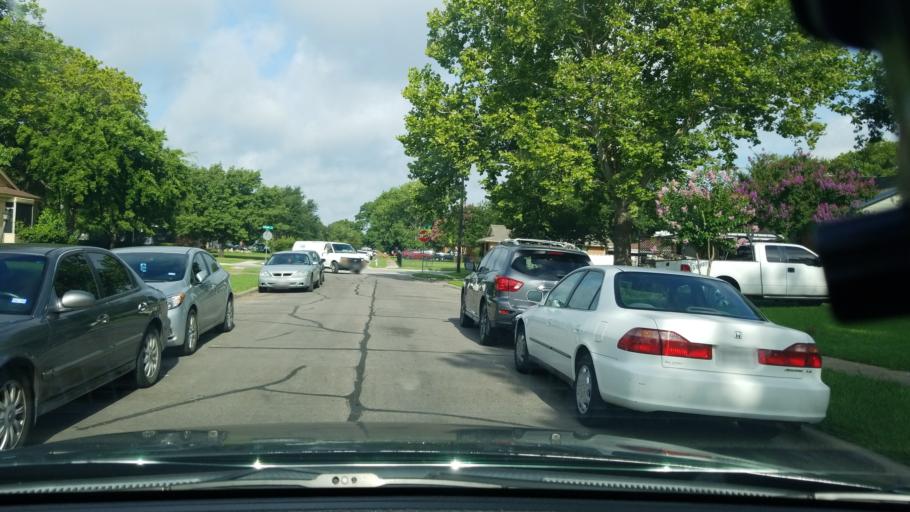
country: US
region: Texas
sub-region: Dallas County
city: Mesquite
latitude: 32.8189
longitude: -96.6678
